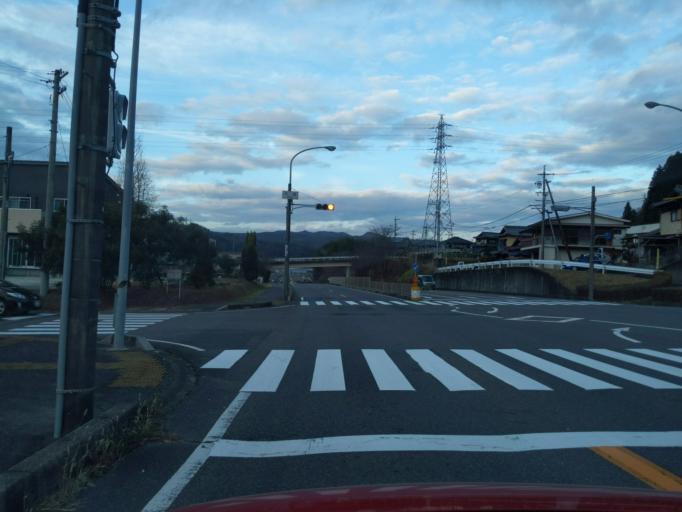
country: JP
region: Gifu
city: Mizunami
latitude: 35.3752
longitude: 137.2666
